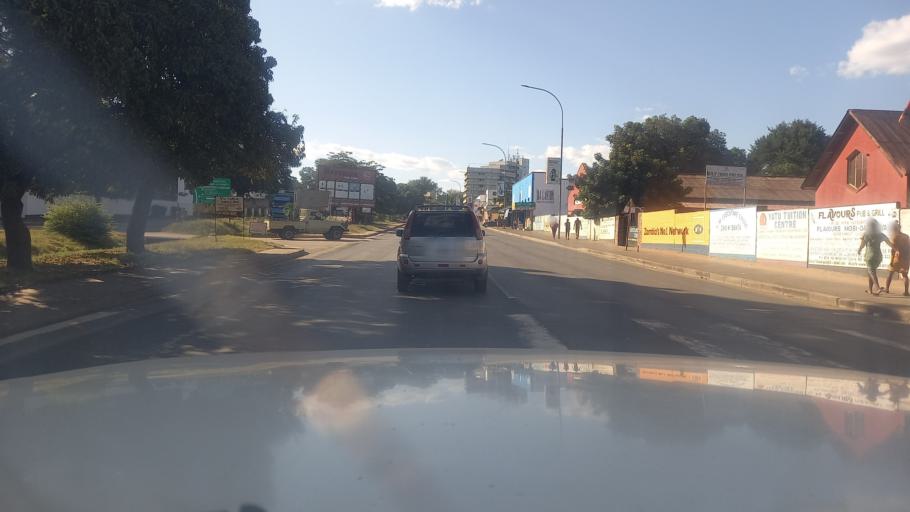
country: ZM
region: Southern
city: Livingstone
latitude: -17.8523
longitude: 25.8552
